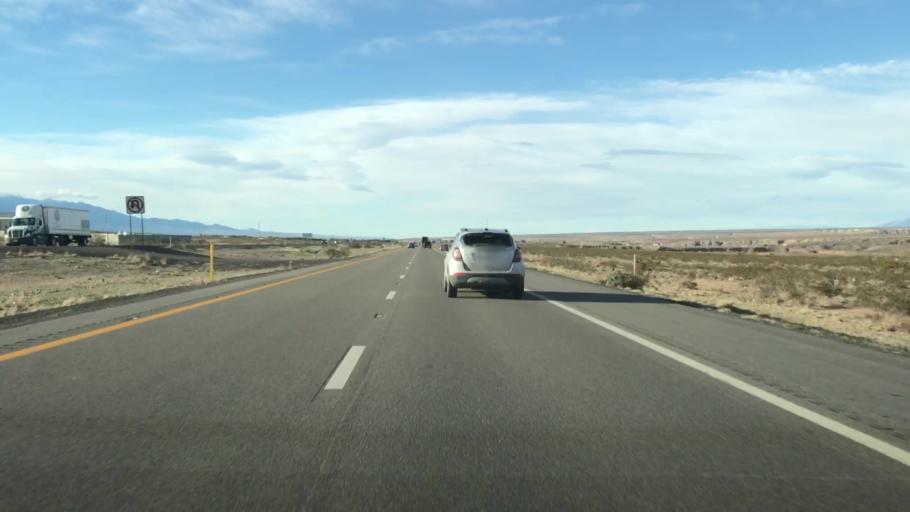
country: US
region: Arizona
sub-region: Mohave County
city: Beaver Dam
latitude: 36.9151
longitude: -113.8821
